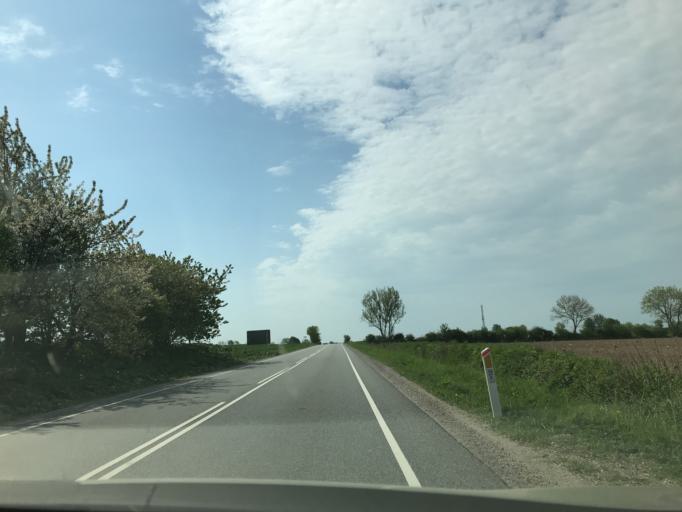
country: DK
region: South Denmark
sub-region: Middelfart Kommune
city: Ejby
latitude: 55.3828
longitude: 9.9179
